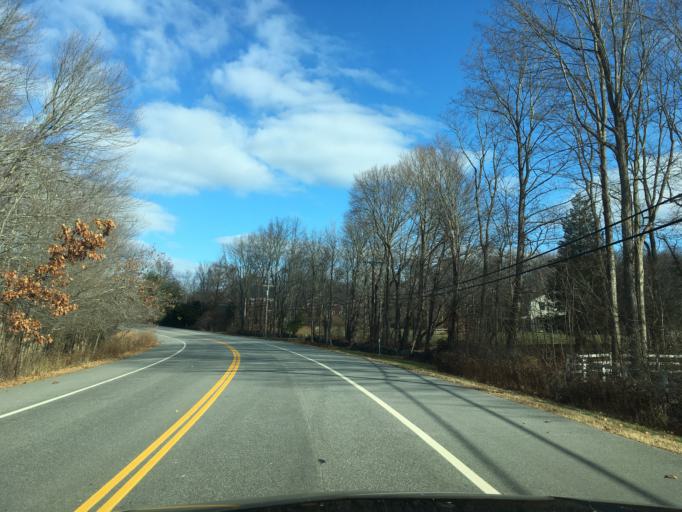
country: US
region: New Hampshire
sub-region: Rockingham County
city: Stratham Station
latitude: 43.0331
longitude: -70.9057
